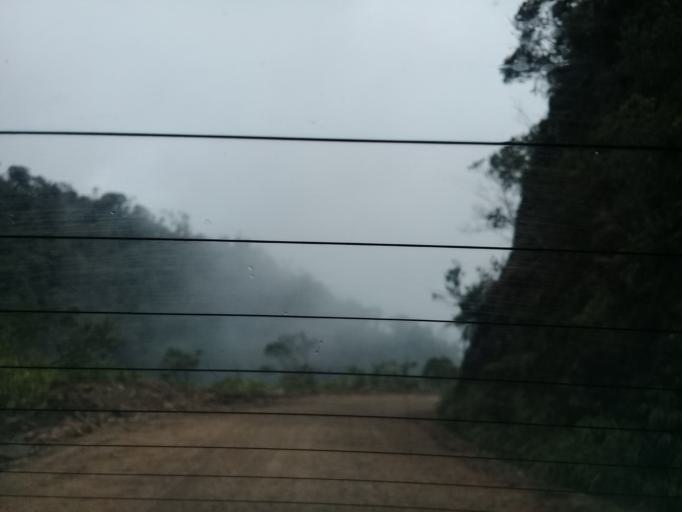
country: CO
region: Cundinamarca
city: Gachala
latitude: 4.6985
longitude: -73.4144
